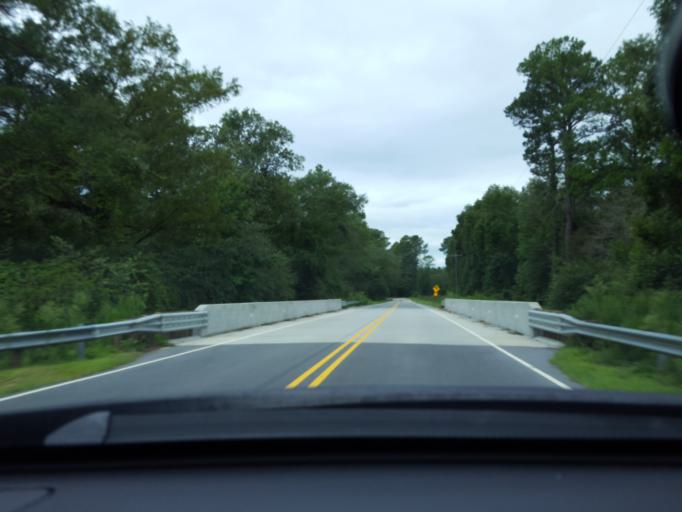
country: US
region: North Carolina
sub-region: Sampson County
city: Clinton
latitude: 34.7933
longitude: -78.3108
